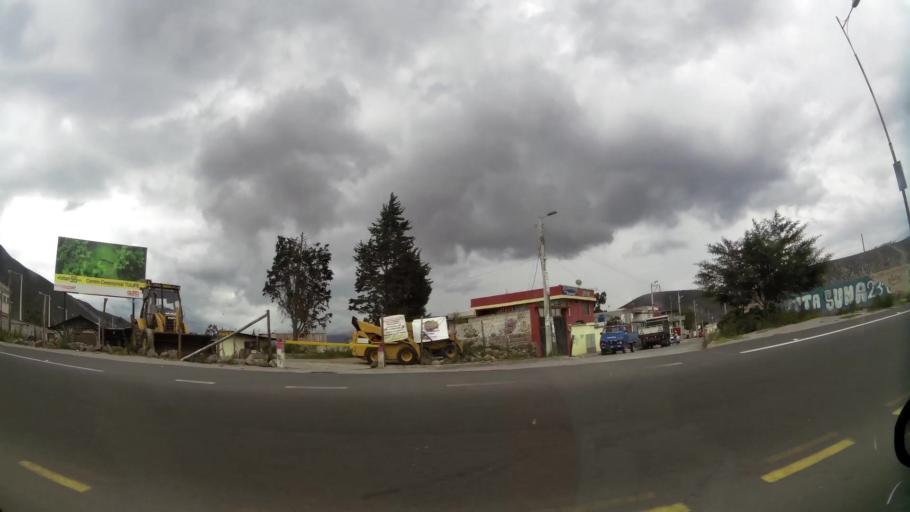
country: EC
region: Pichincha
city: Quito
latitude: -0.0008
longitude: -78.4530
